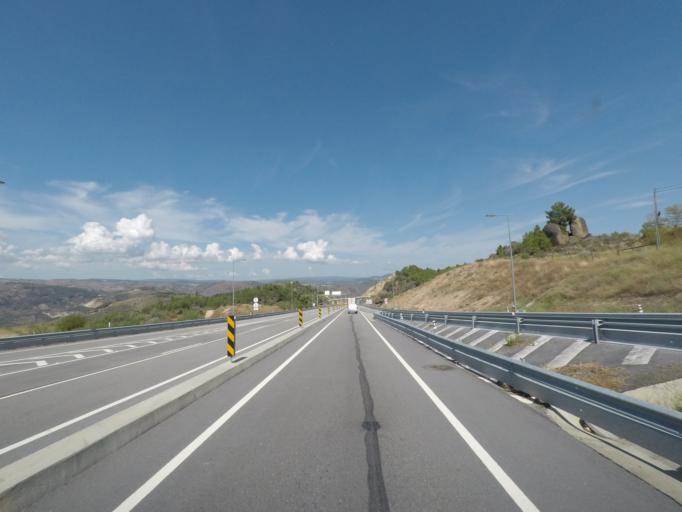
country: PT
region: Braganca
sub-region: Carrazeda de Ansiaes
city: Carrazeda de Anciaes
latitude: 41.3055
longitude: -7.3437
